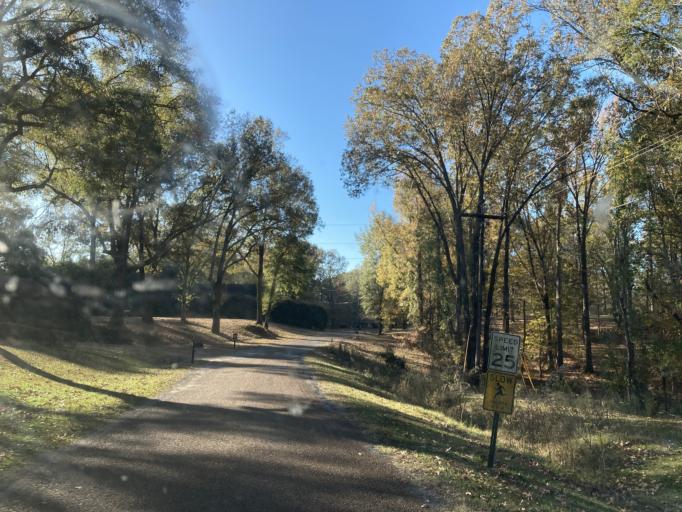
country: US
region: Mississippi
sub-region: Yazoo County
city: Yazoo City
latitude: 32.7947
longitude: -90.3559
